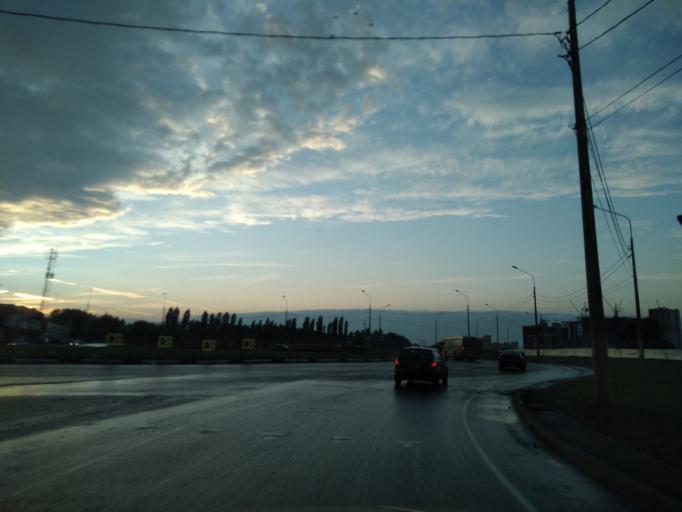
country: RU
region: Lipetsk
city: Syrskoye
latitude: 52.5711
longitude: 39.5161
